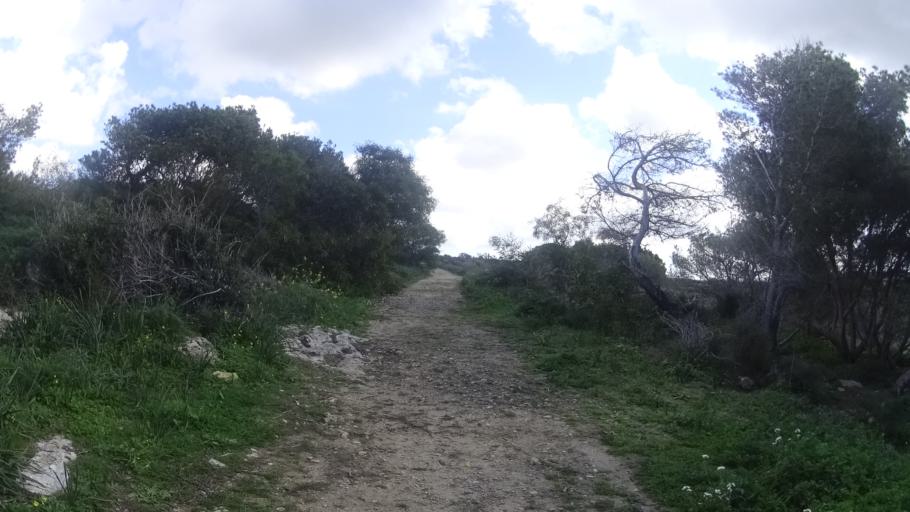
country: MT
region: L-Imgarr
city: Imgarr
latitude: 35.9042
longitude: 14.3784
